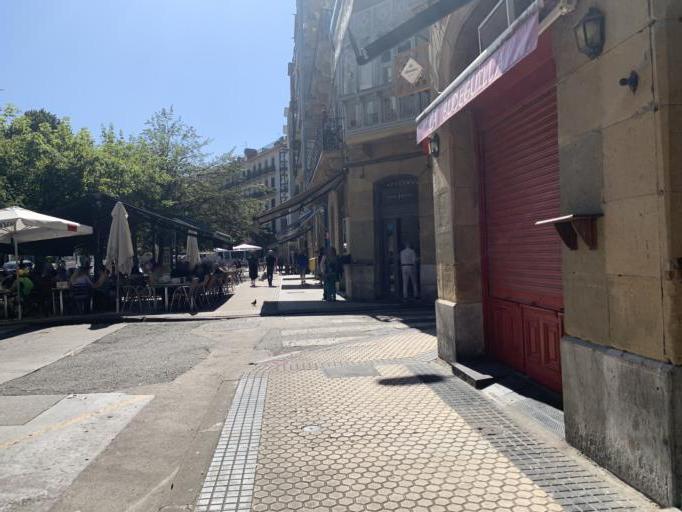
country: ES
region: Basque Country
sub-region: Provincia de Guipuzcoa
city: San Sebastian
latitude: 43.3145
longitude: -1.9823
